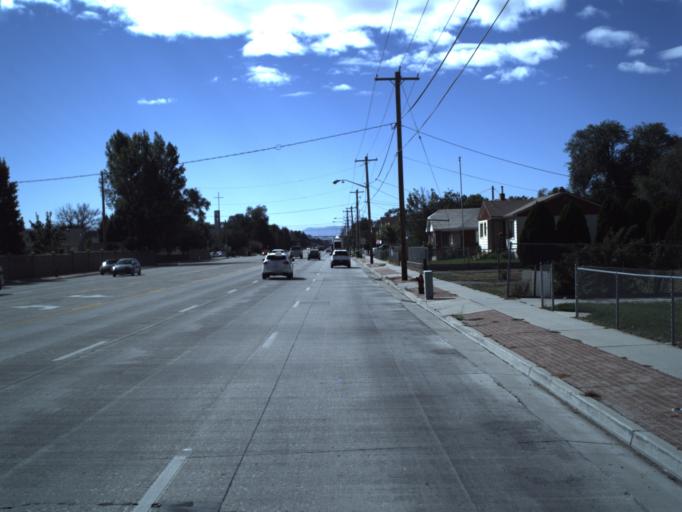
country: US
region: Utah
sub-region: Salt Lake County
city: West Jordan
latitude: 40.6197
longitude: -111.9389
